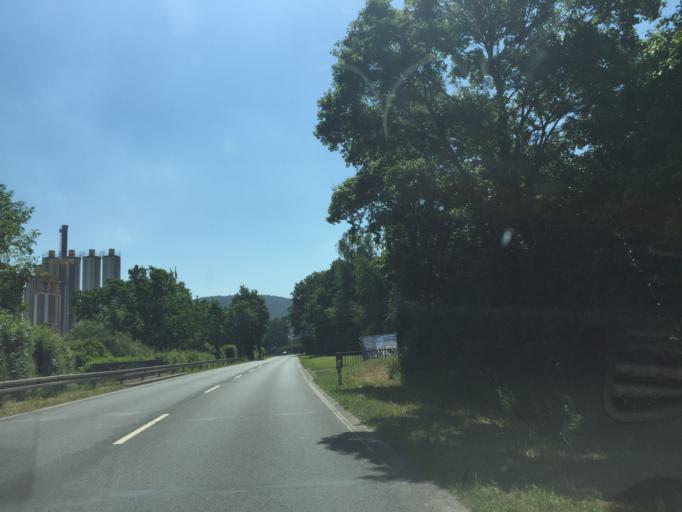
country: DE
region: Bavaria
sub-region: Regierungsbezirk Unterfranken
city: Weilbach
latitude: 49.6438
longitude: 9.2270
